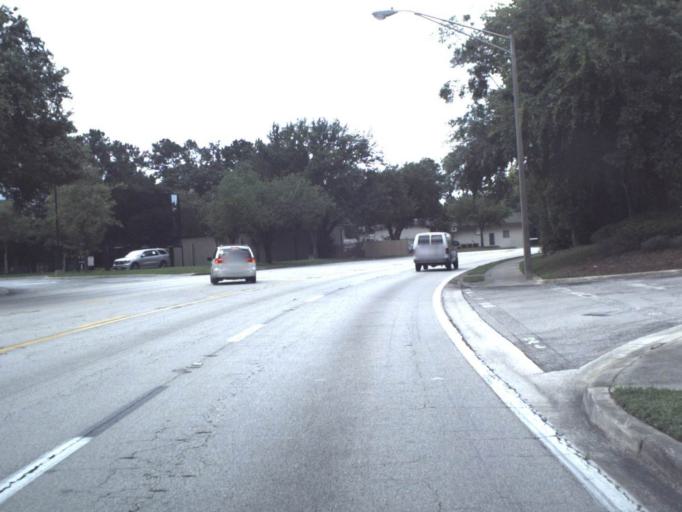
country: US
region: Florida
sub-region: Duval County
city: Jacksonville
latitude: 30.2920
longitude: -81.6163
